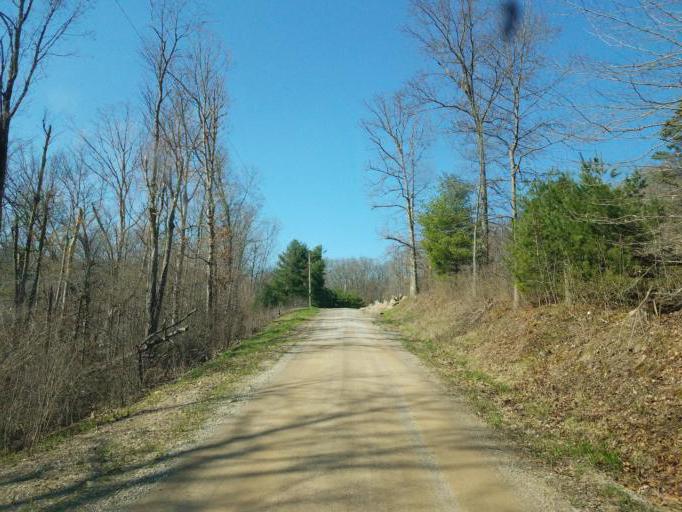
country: US
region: Ohio
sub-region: Knox County
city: Oak Hill
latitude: 40.3889
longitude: -82.1998
